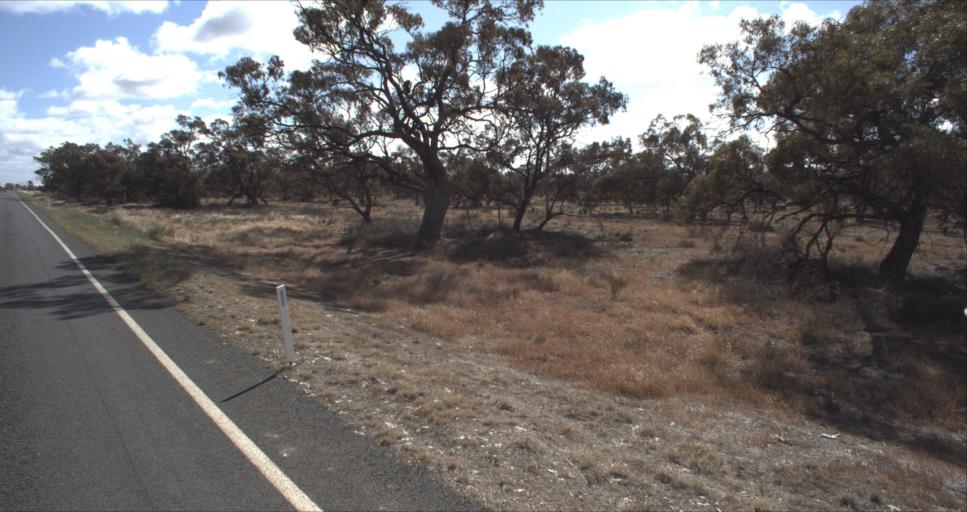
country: AU
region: New South Wales
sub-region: Murrumbidgee Shire
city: Darlington Point
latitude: -34.5241
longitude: 146.1752
